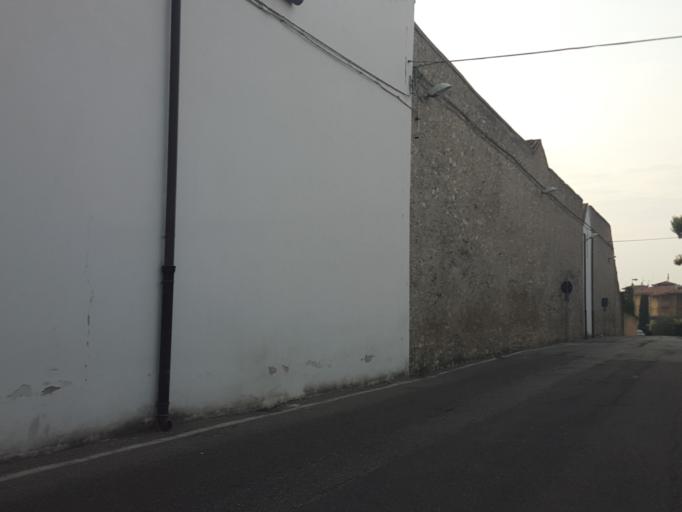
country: IT
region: Veneto
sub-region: Provincia di Verona
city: Garda
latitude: 45.5758
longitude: 10.7129
